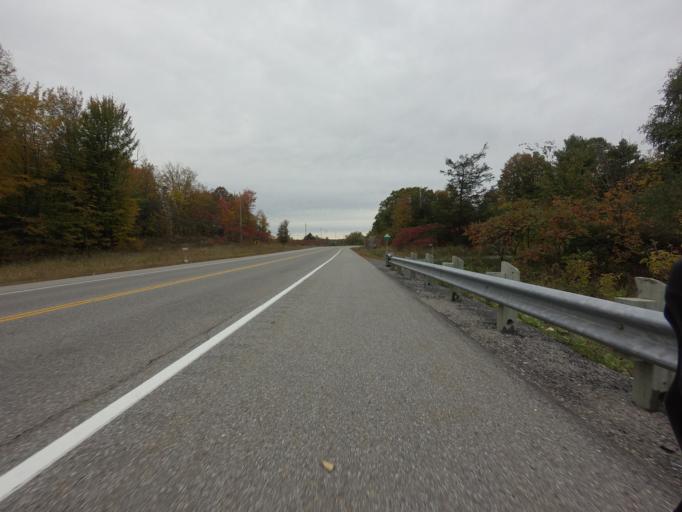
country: CA
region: Ontario
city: Gananoque
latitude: 44.4525
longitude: -76.2668
